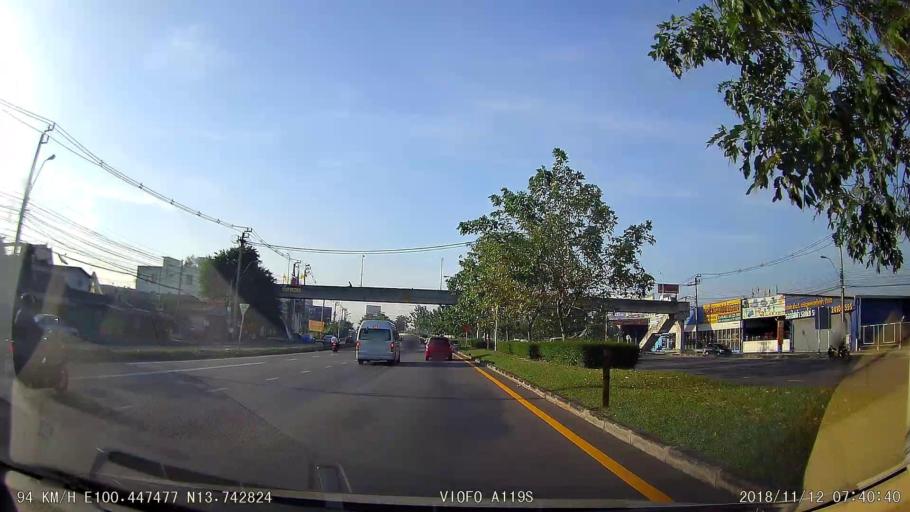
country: TH
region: Bangkok
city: Phasi Charoen
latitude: 13.7426
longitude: 100.4474
